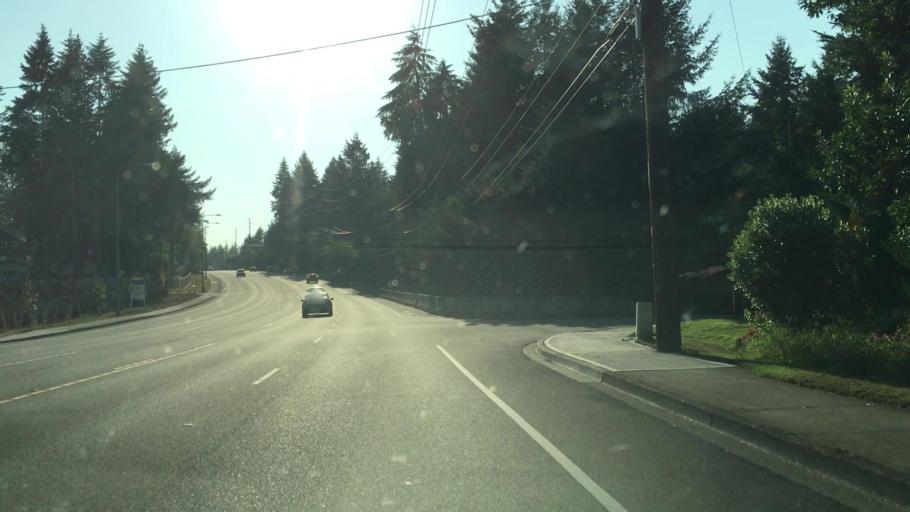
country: US
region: Washington
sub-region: Pierce County
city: Fife Heights
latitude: 47.2827
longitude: -122.3370
